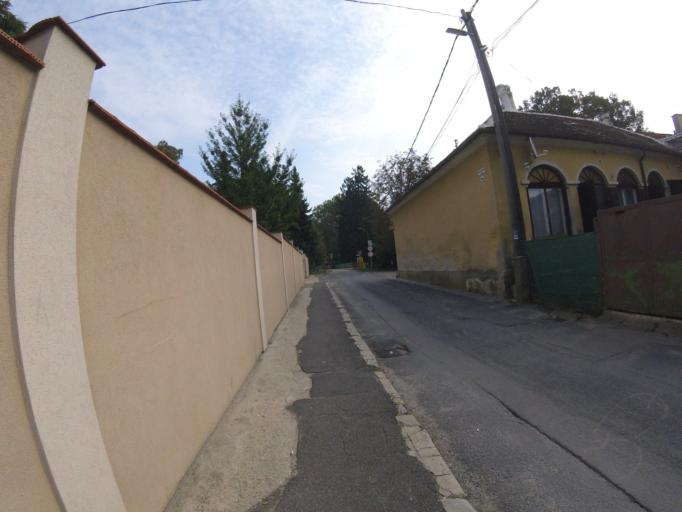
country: HU
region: Vas
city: Koszeg
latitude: 47.3911
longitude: 16.5457
